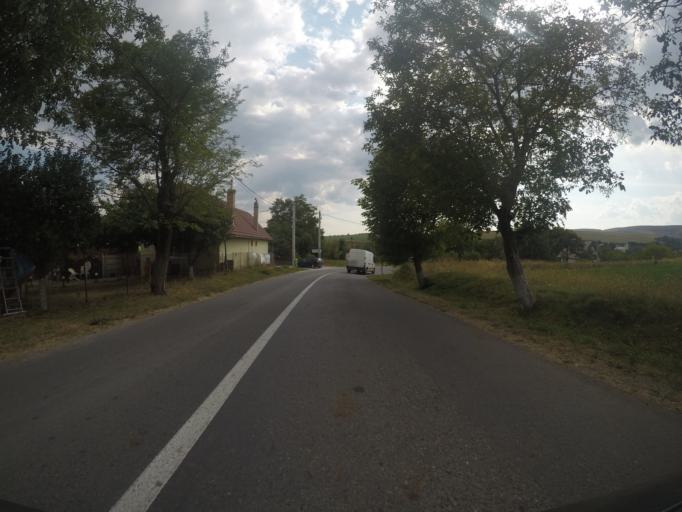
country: RO
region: Cluj
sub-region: Comuna Sandulesti
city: Sandulesti
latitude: 46.5814
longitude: 23.7312
